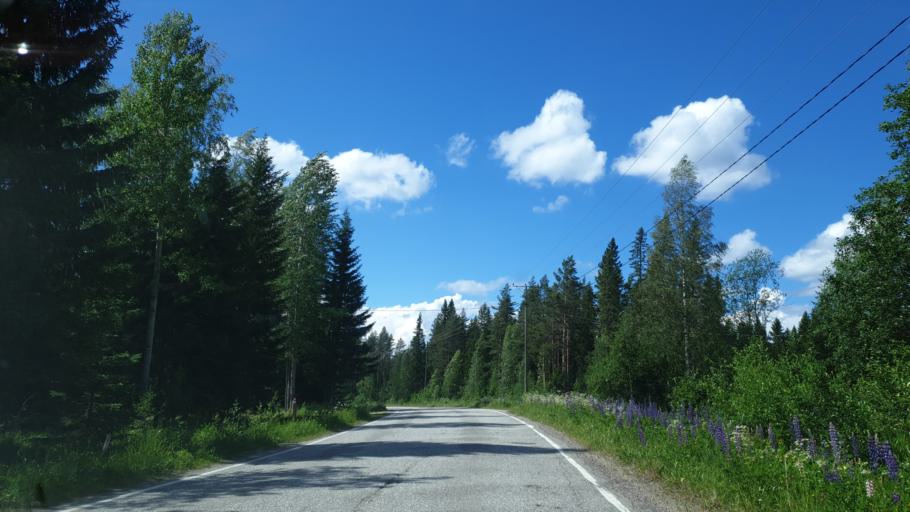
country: FI
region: Northern Savo
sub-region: Koillis-Savo
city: Kaavi
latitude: 63.0423
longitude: 28.5888
